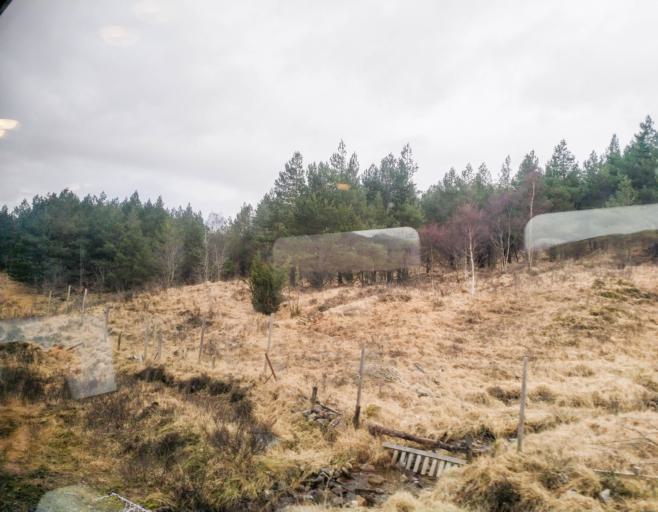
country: GB
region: Scotland
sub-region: Highland
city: Spean Bridge
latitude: 56.5307
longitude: -4.7630
